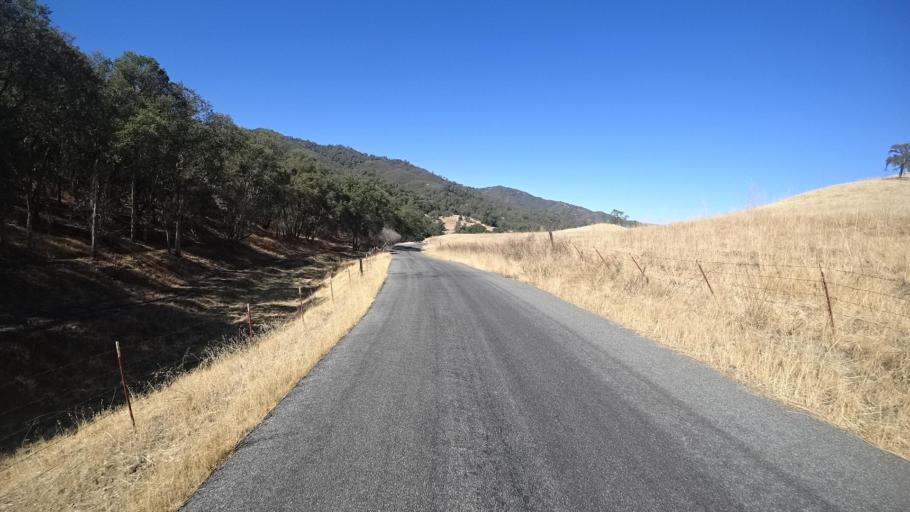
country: US
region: California
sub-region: Monterey County
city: Gonzales
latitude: 36.3377
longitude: -121.5300
